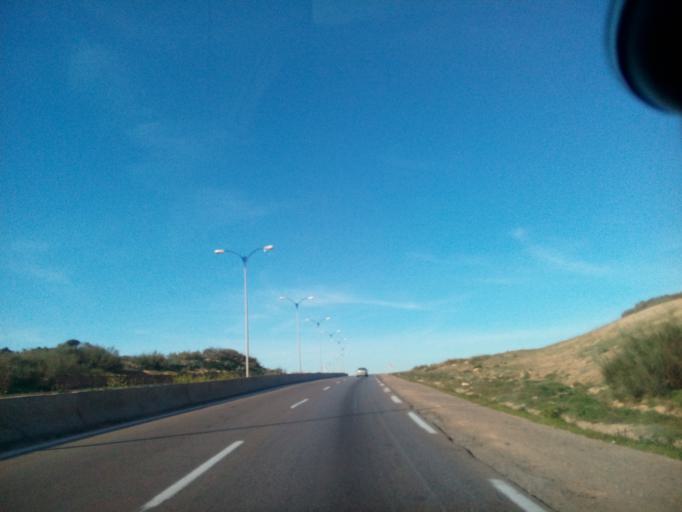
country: DZ
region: Oran
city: Ain el Bya
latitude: 35.7867
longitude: -0.1093
